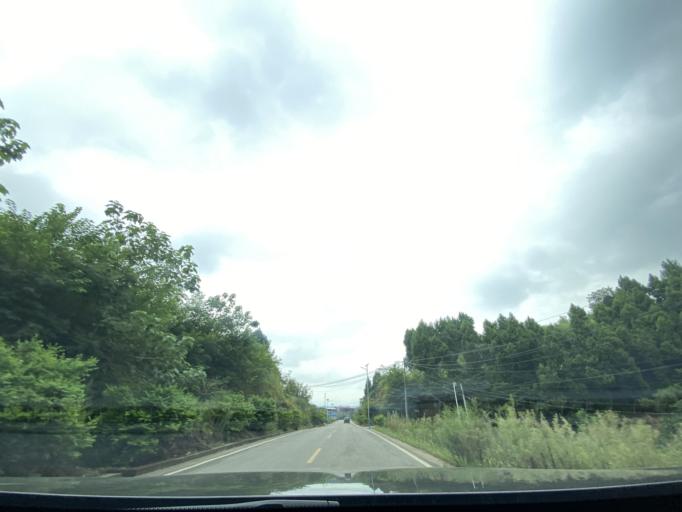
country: CN
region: Sichuan
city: Jiancheng
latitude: 30.5393
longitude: 104.5232
